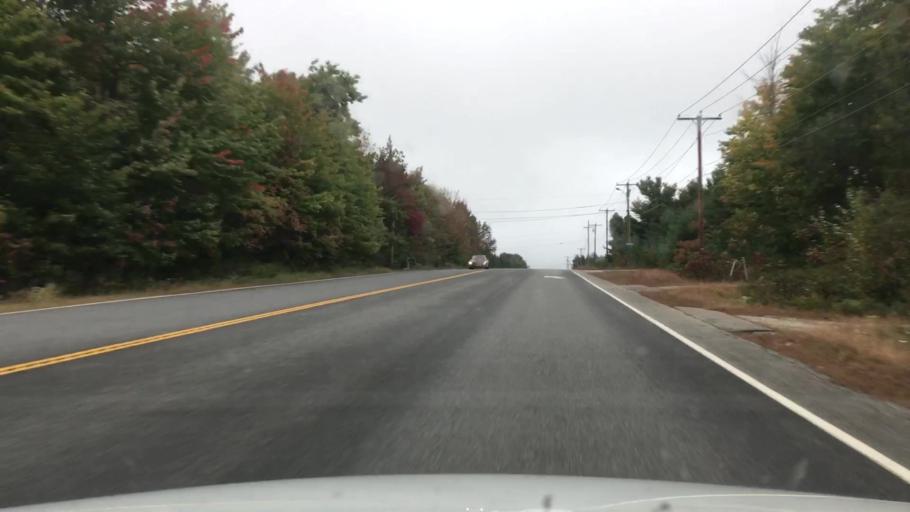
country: US
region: Maine
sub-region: Androscoggin County
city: Poland
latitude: 44.0019
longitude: -70.3640
